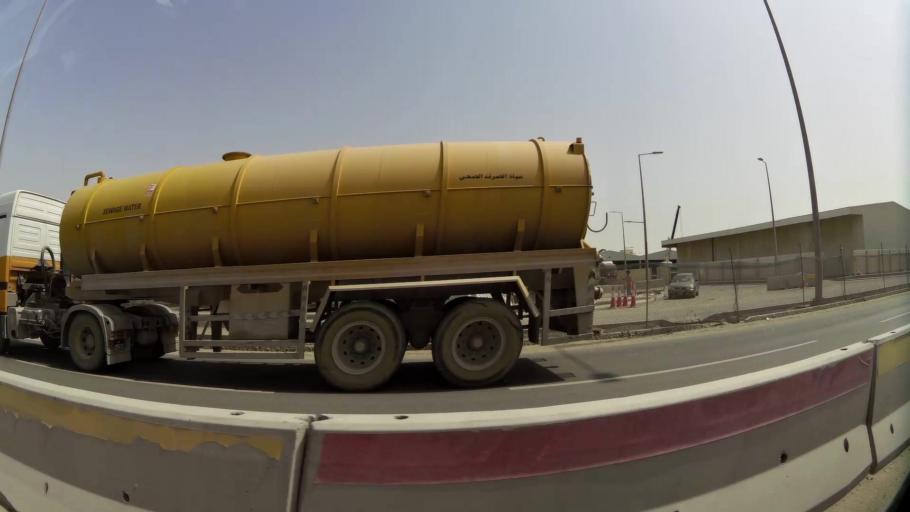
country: QA
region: Baladiyat ar Rayyan
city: Ar Rayyan
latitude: 25.1888
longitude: 51.4211
